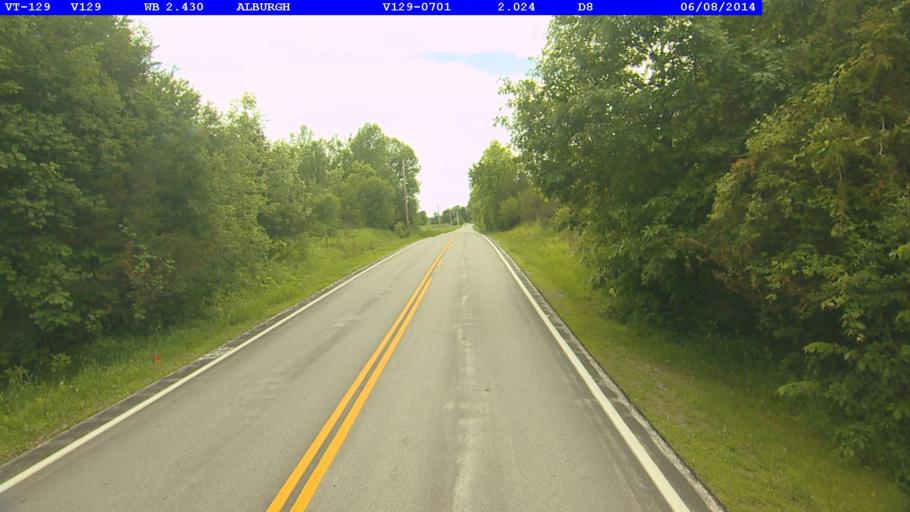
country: US
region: Vermont
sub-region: Grand Isle County
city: North Hero
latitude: 44.8874
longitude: -73.2939
